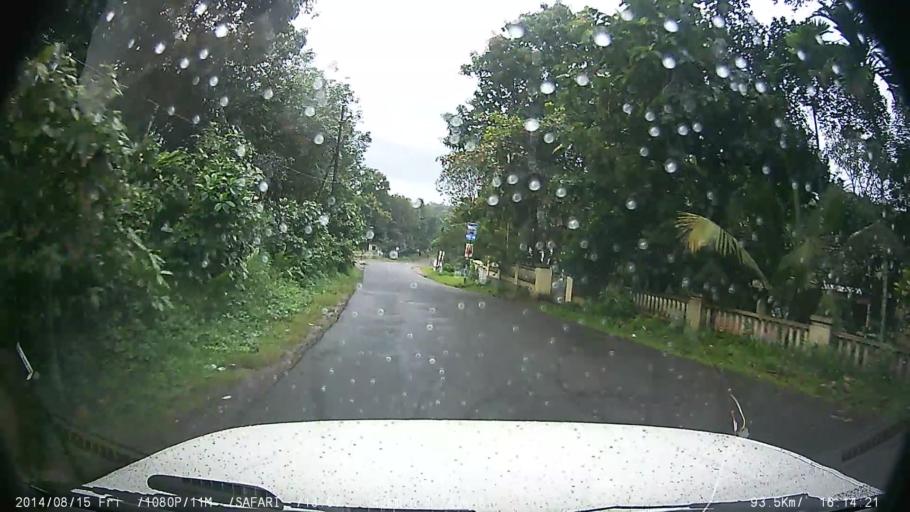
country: IN
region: Kerala
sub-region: Kottayam
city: Lalam
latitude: 9.7365
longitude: 76.6916
